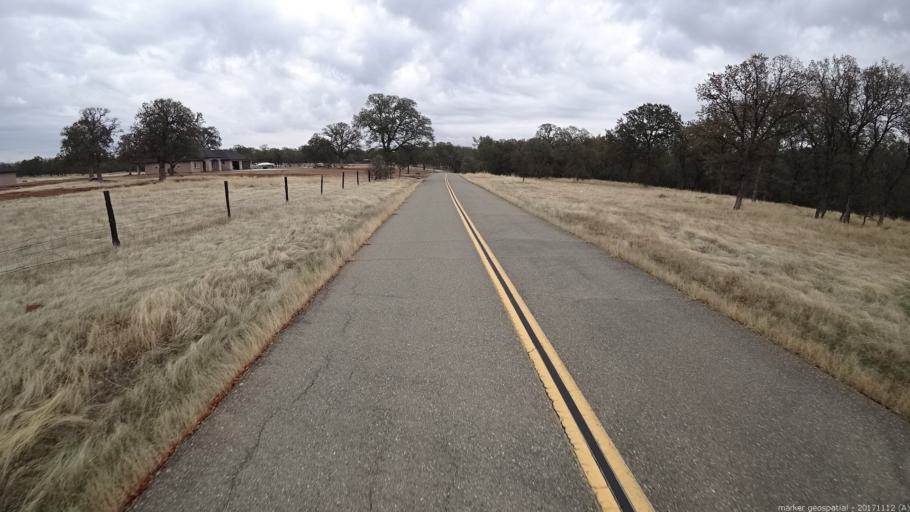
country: US
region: California
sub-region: Shasta County
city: Palo Cedro
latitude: 40.4799
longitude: -122.2098
